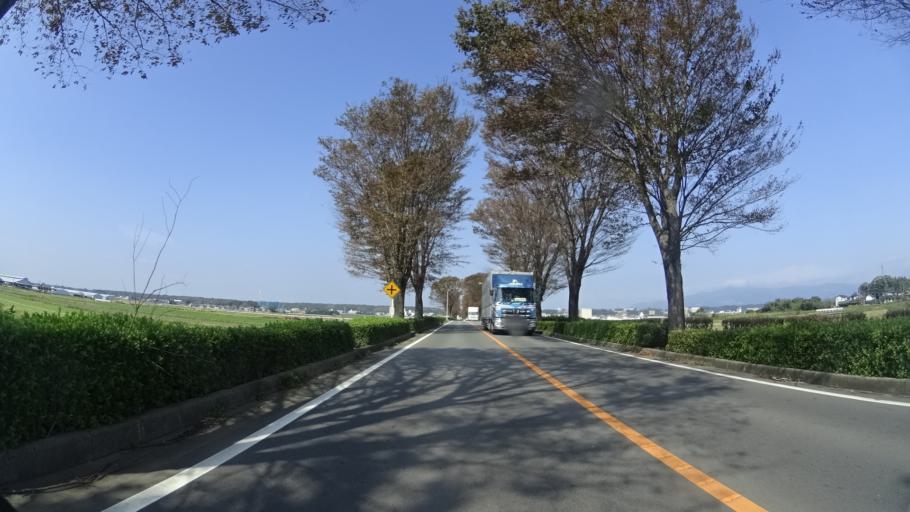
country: JP
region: Kumamoto
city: Ozu
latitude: 32.8630
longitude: 130.8553
